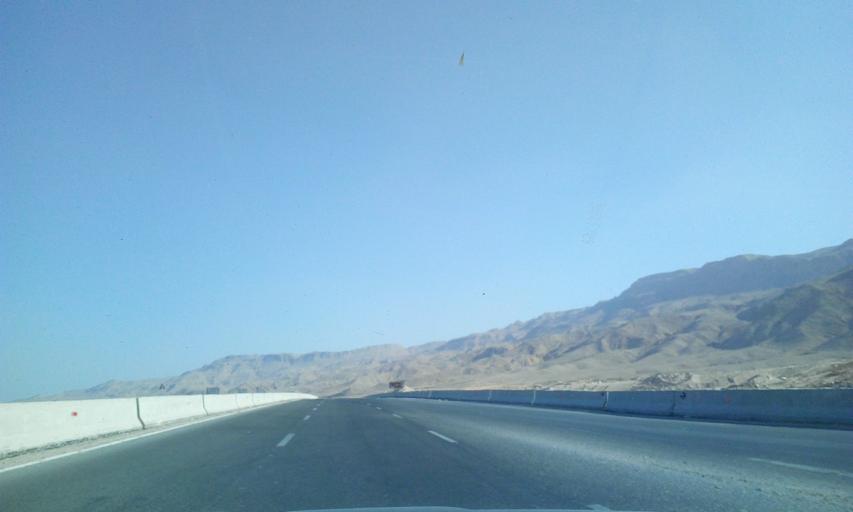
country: EG
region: As Suways
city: Ain Sukhna
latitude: 29.4076
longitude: 32.3984
